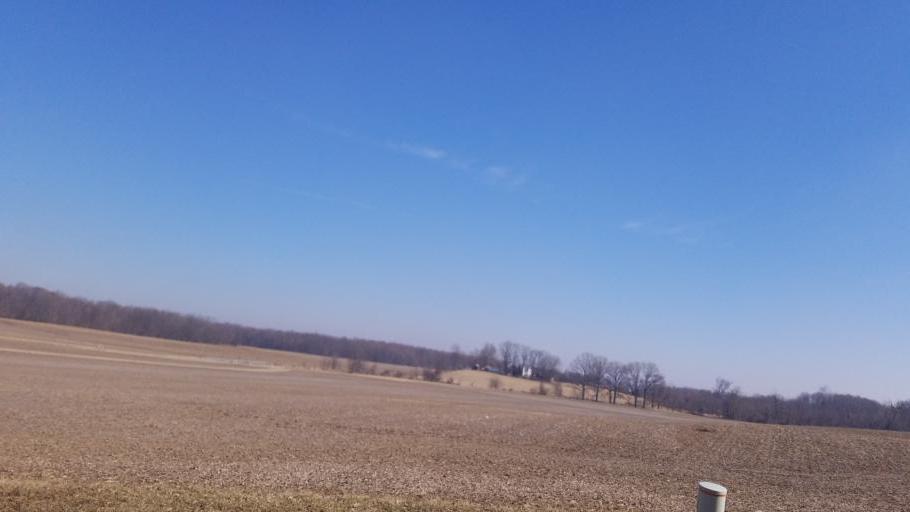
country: US
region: Ohio
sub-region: Richland County
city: Lincoln Heights
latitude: 40.8662
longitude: -82.5325
